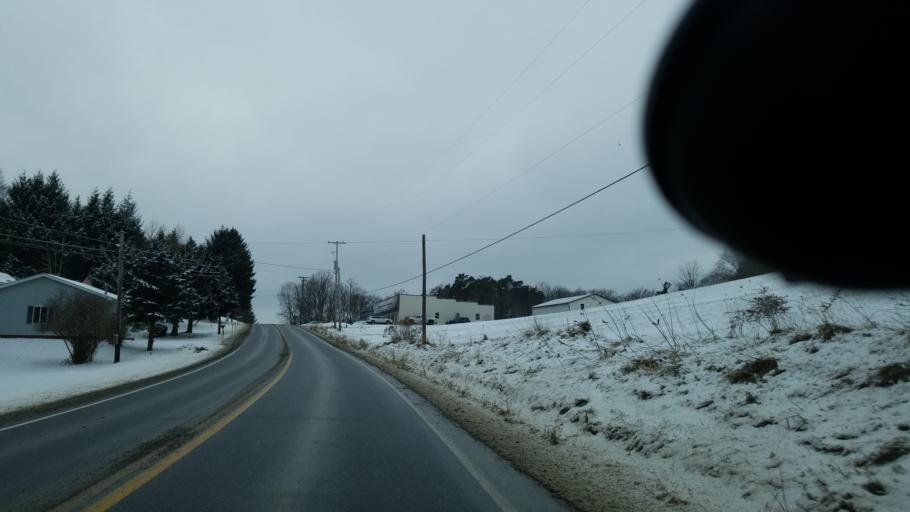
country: US
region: Pennsylvania
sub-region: Jefferson County
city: Albion
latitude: 40.9387
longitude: -78.9456
